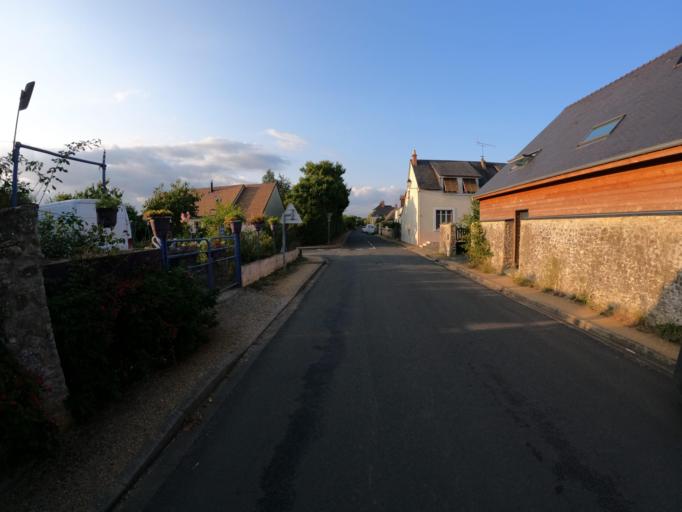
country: FR
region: Pays de la Loire
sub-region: Departement de la Sarthe
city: Brulon
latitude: 47.9491
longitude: -0.2226
